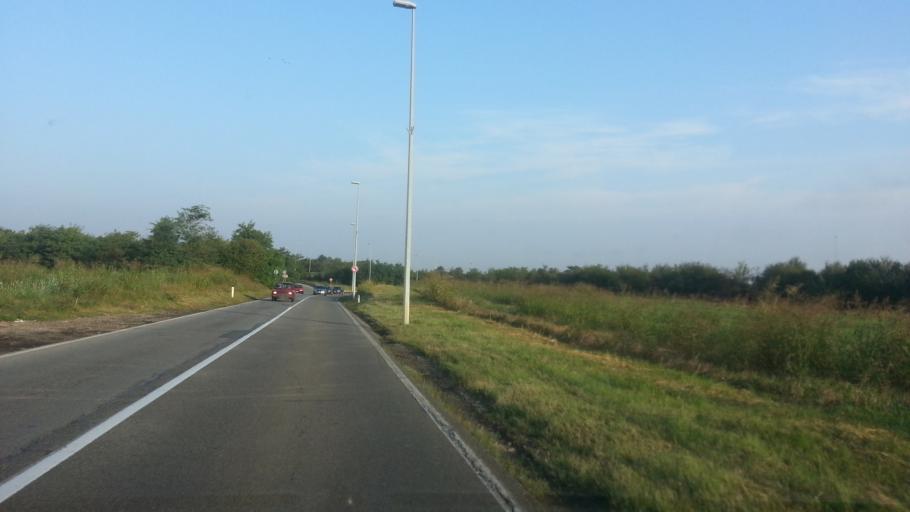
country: RS
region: Central Serbia
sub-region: Belgrade
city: Surcin
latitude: 44.8317
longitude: 20.2783
